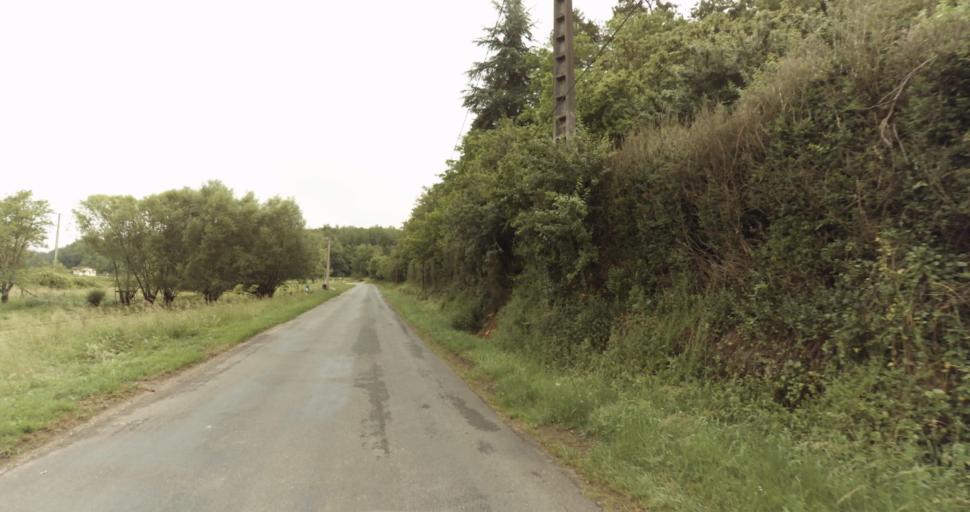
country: FR
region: Aquitaine
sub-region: Departement de la Dordogne
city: Lalinde
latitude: 44.8784
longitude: 0.7782
